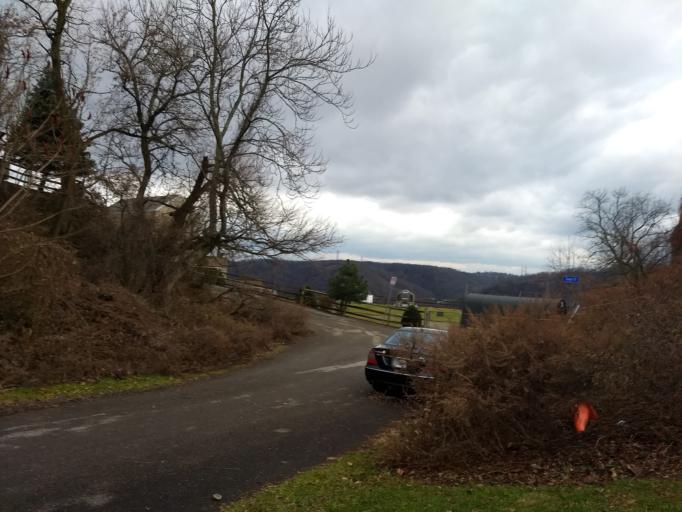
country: US
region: Pennsylvania
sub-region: Allegheny County
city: Homestead
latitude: 40.4203
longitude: -79.9461
